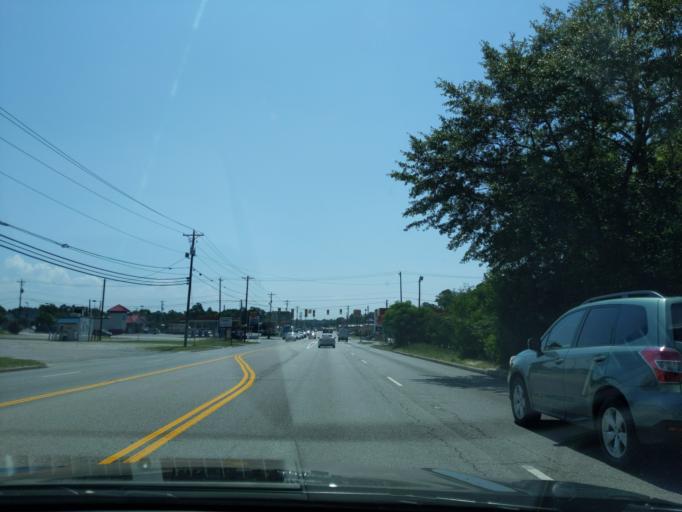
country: US
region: South Carolina
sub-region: Lexington County
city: Oak Grove
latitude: 33.9742
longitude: -81.1579
